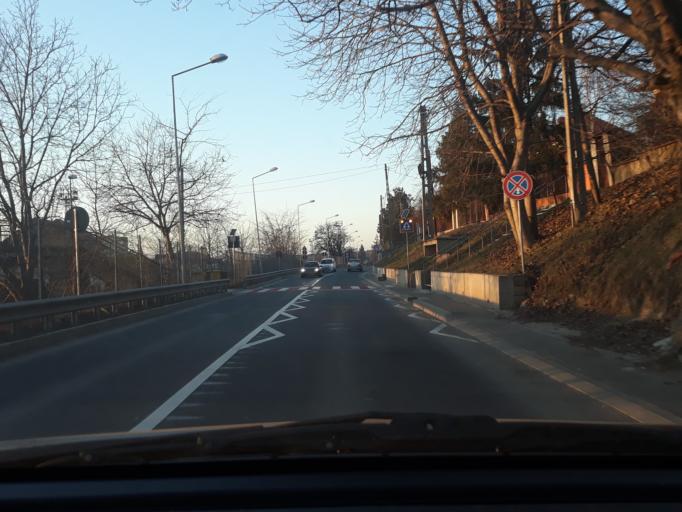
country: RO
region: Bihor
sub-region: Comuna Biharea
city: Oradea
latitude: 47.0666
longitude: 21.9386
